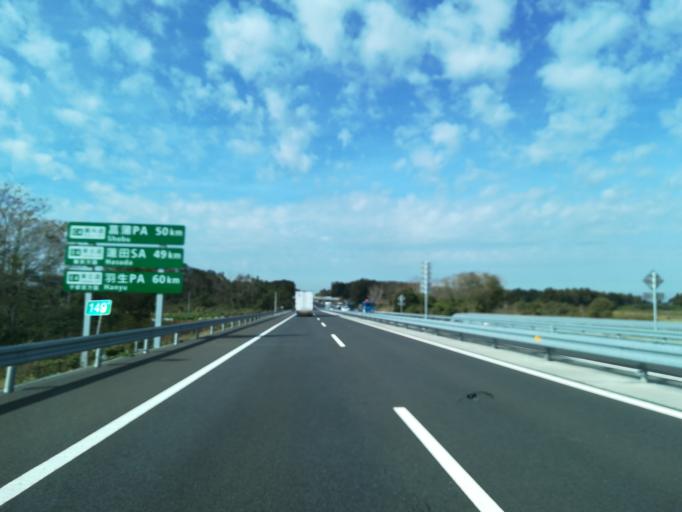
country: JP
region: Ibaraki
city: Mitsukaido
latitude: 36.0617
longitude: 140.0367
